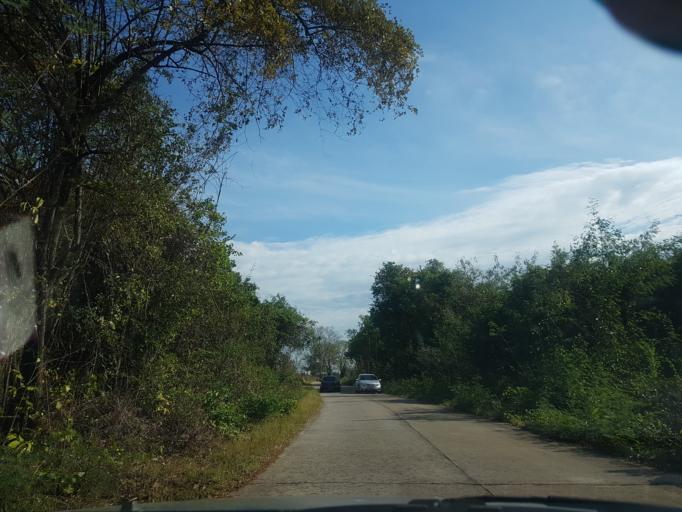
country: TH
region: Lop Buri
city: Lop Buri
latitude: 14.8228
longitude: 100.7545
